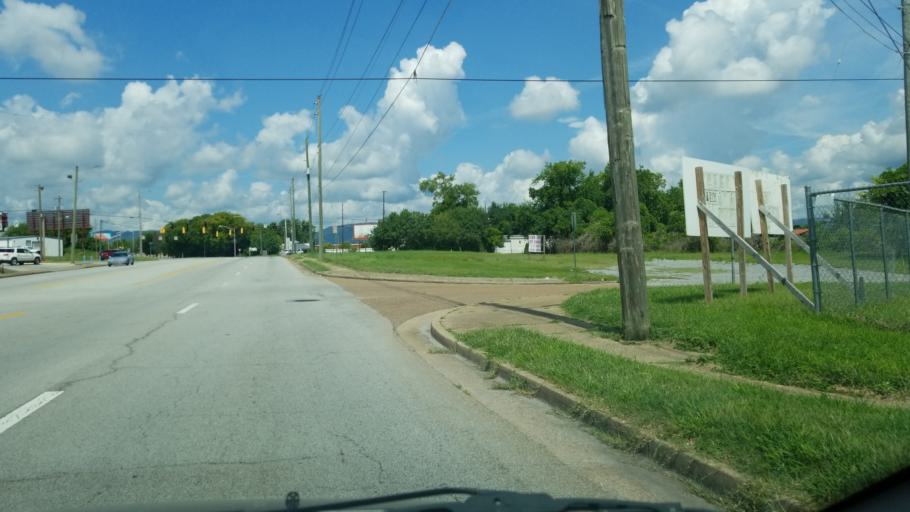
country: US
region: Tennessee
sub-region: Hamilton County
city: Chattanooga
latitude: 35.0240
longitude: -85.2963
